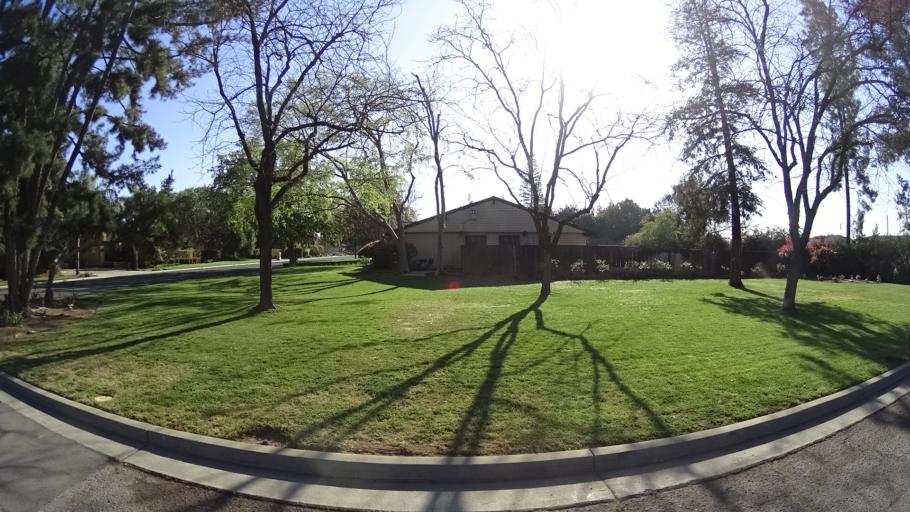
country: US
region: California
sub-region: Fresno County
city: Fresno
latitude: 36.8253
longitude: -119.8308
